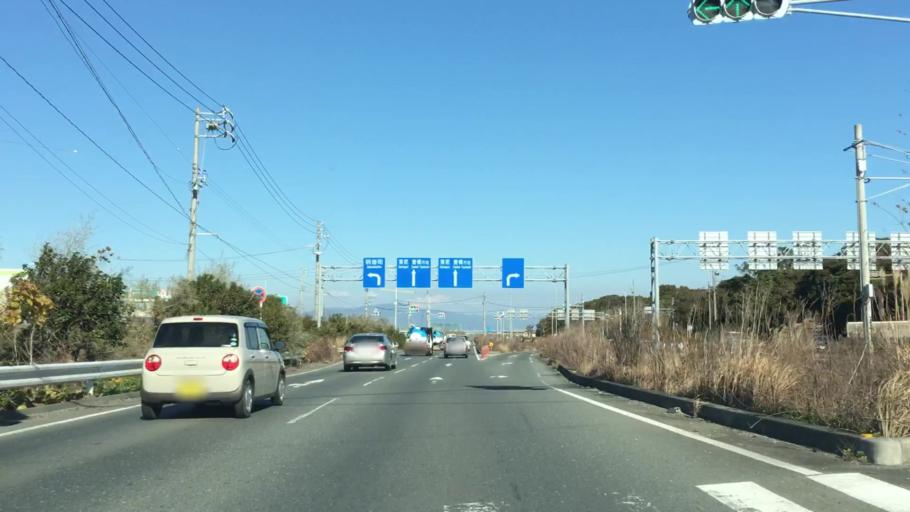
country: JP
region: Aichi
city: Toyohashi
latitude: 34.7189
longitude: 137.3403
